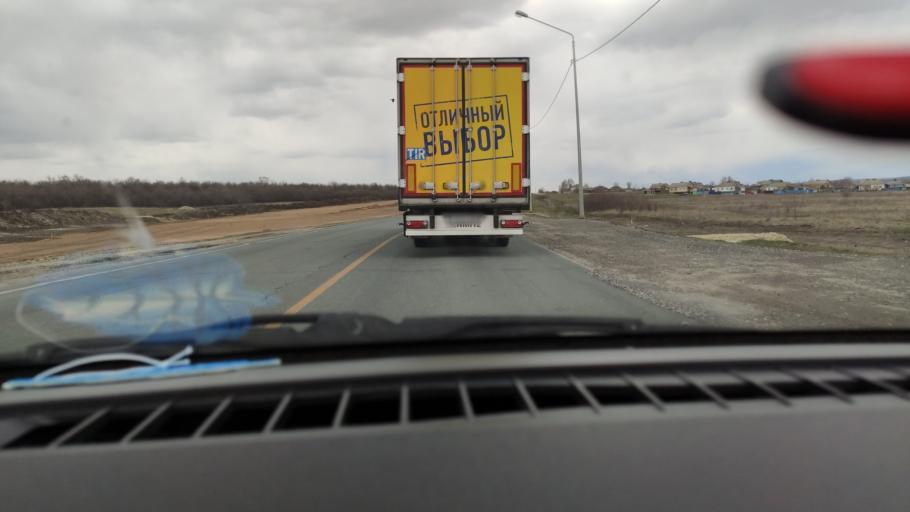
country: RU
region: Saratov
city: Sennoy
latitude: 52.1584
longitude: 47.0681
